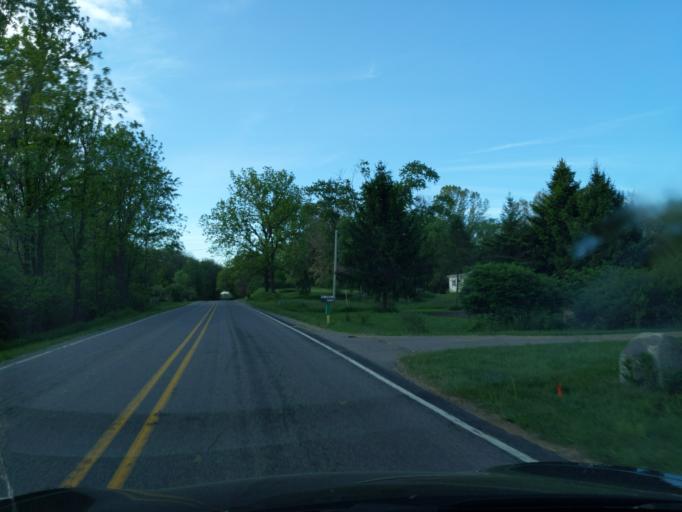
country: US
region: Michigan
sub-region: Ingham County
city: Leslie
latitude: 42.4802
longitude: -84.3170
